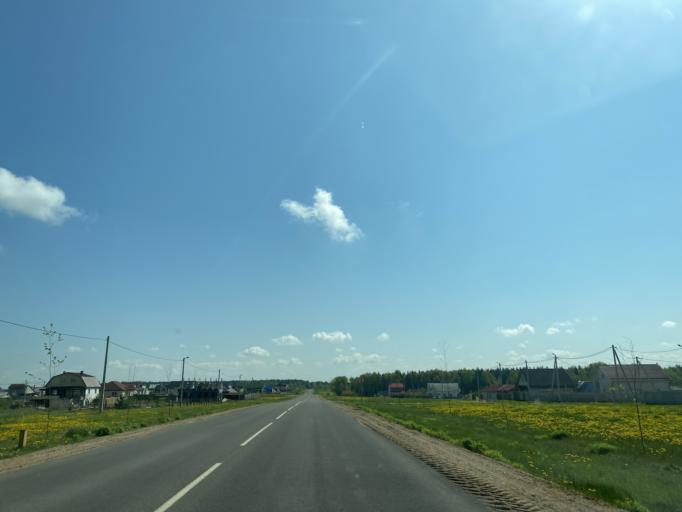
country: BY
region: Minsk
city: Horad Barysaw
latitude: 54.1786
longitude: 28.5507
